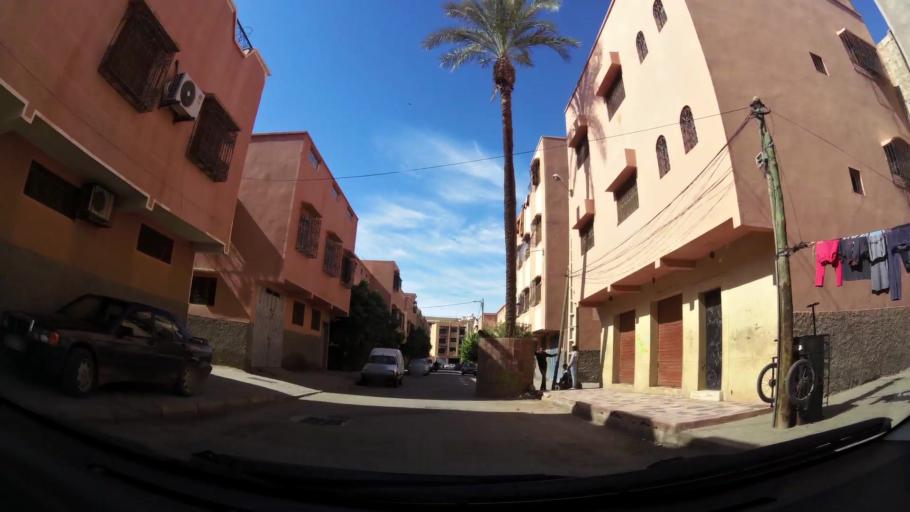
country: MA
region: Marrakech-Tensift-Al Haouz
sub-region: Marrakech
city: Marrakesh
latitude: 31.6439
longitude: -7.9790
